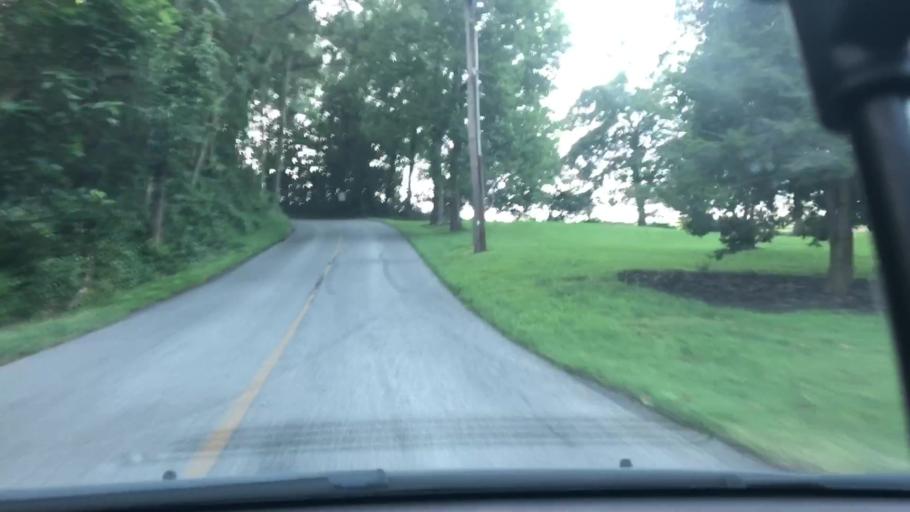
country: US
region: Pennsylvania
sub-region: Chester County
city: Kenilworth
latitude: 40.1896
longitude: -75.6468
